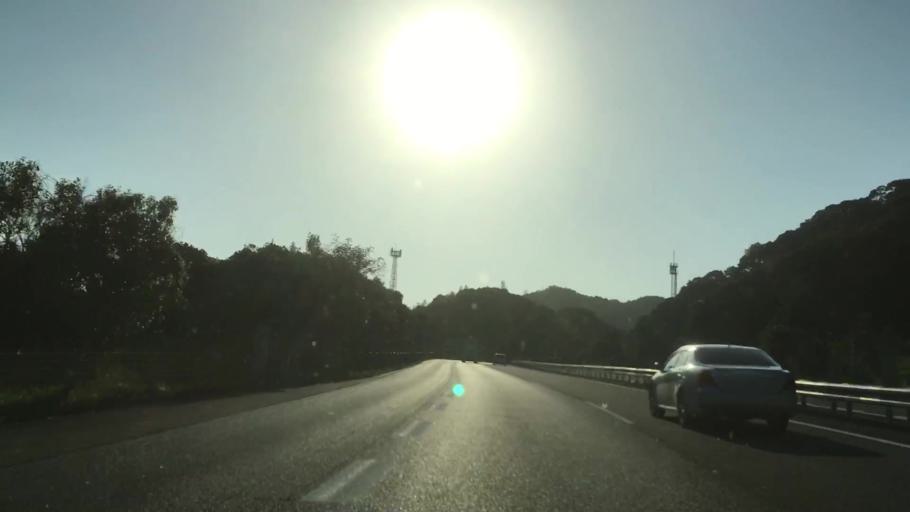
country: JP
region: Yamaguchi
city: Ogori-shimogo
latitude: 34.1364
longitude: 131.3699
